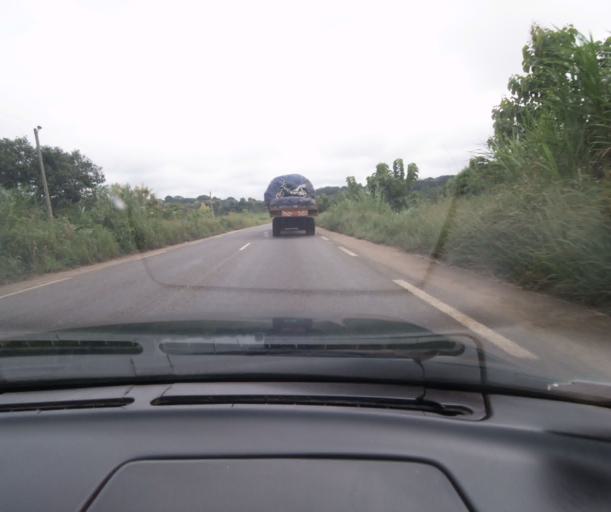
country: CM
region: Centre
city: Ombesa
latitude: 4.5795
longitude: 11.2661
